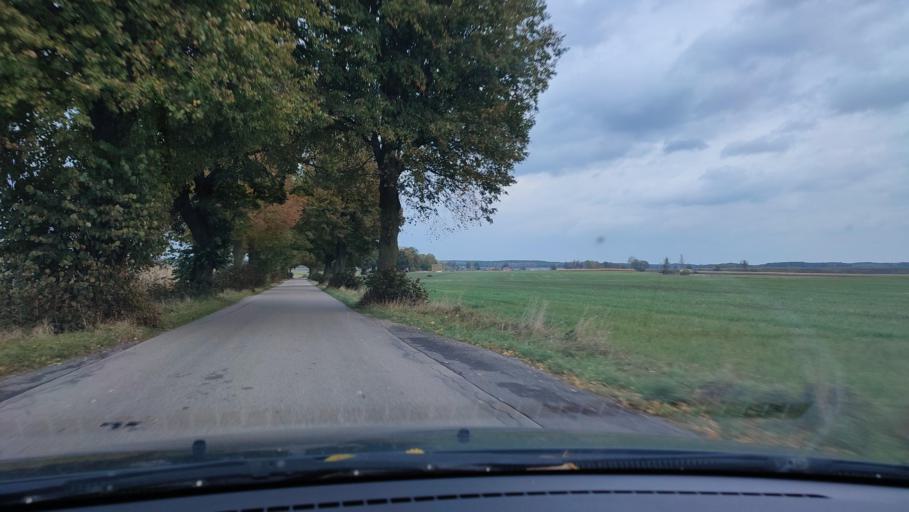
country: PL
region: Masovian Voivodeship
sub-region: Powiat mlawski
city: Wieczfnia Koscielna
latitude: 53.2213
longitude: 20.4109
